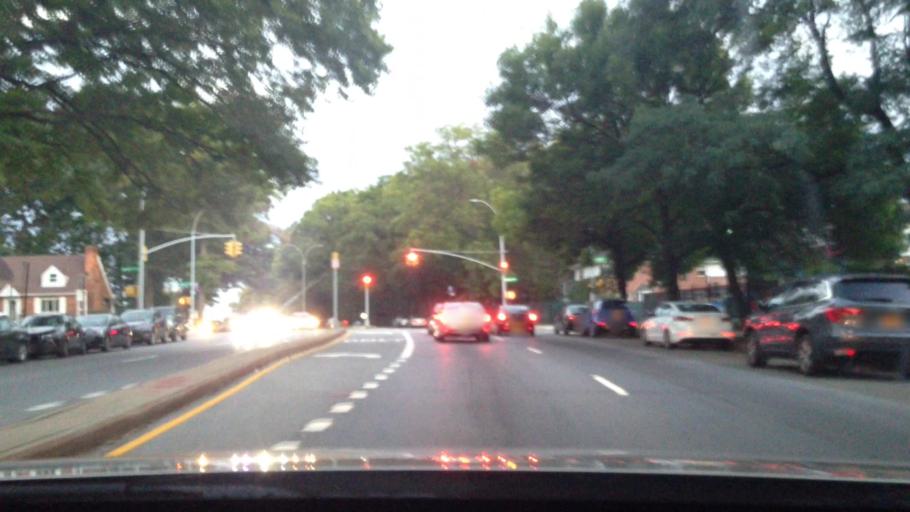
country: US
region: New York
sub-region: Nassau County
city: Bellerose Terrace
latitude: 40.7251
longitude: -73.7653
